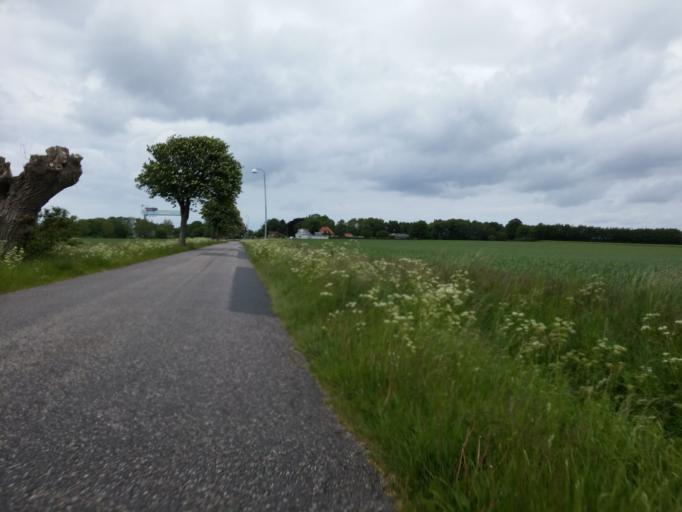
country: DK
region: South Denmark
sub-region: Kerteminde Kommune
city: Munkebo
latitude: 55.4452
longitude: 10.5207
